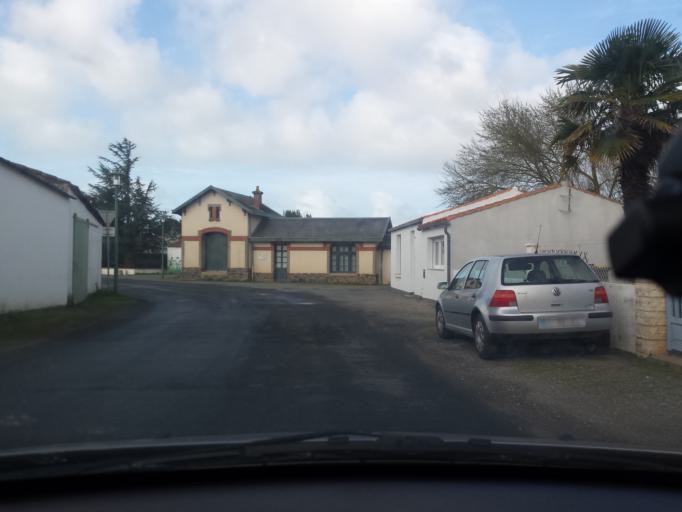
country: FR
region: Pays de la Loire
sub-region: Departement de la Vendee
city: Olonne-sur-Mer
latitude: 46.5631
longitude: -1.7835
